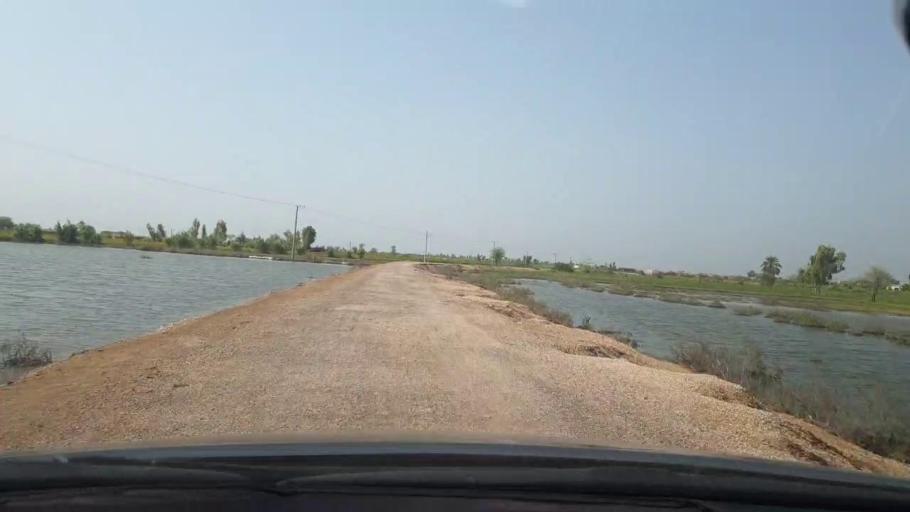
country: PK
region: Sindh
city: Tando Bago
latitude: 24.7121
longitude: 69.0881
